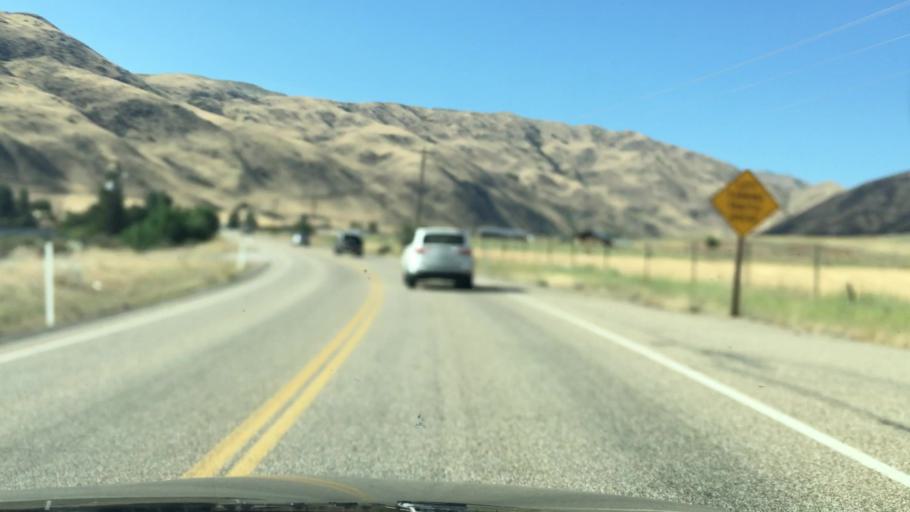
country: US
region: Idaho
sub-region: Gem County
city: Emmett
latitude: 43.9876
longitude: -116.1864
